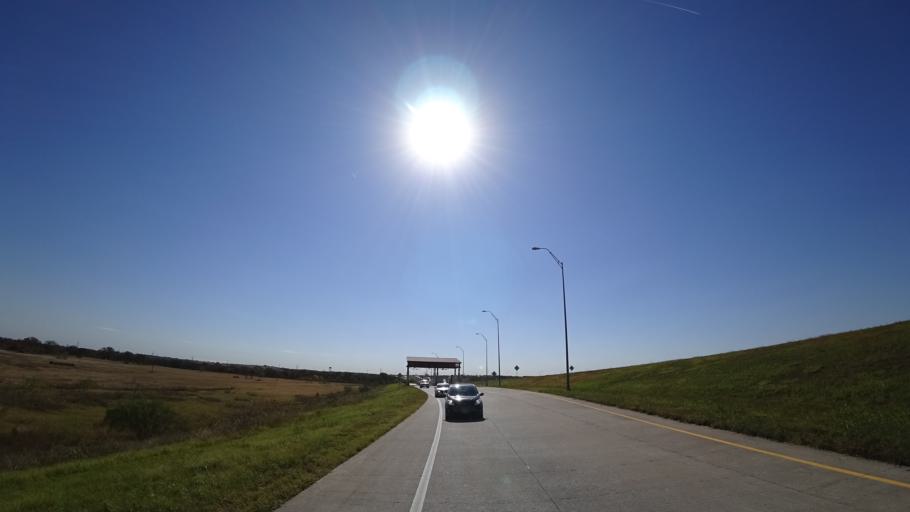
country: US
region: Texas
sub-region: Williamson County
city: Hutto
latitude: 30.5323
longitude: -97.5754
